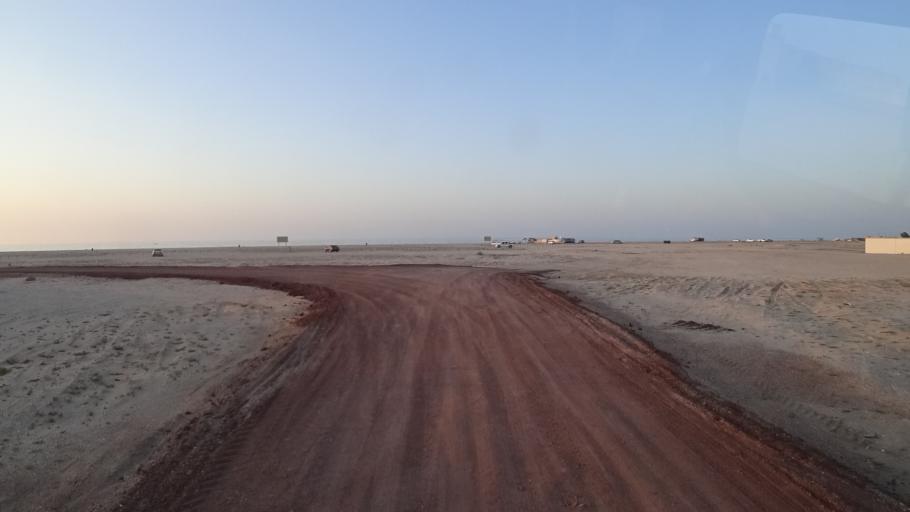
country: OM
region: Ash Sharqiyah
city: Sur
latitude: 22.5305
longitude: 59.7645
